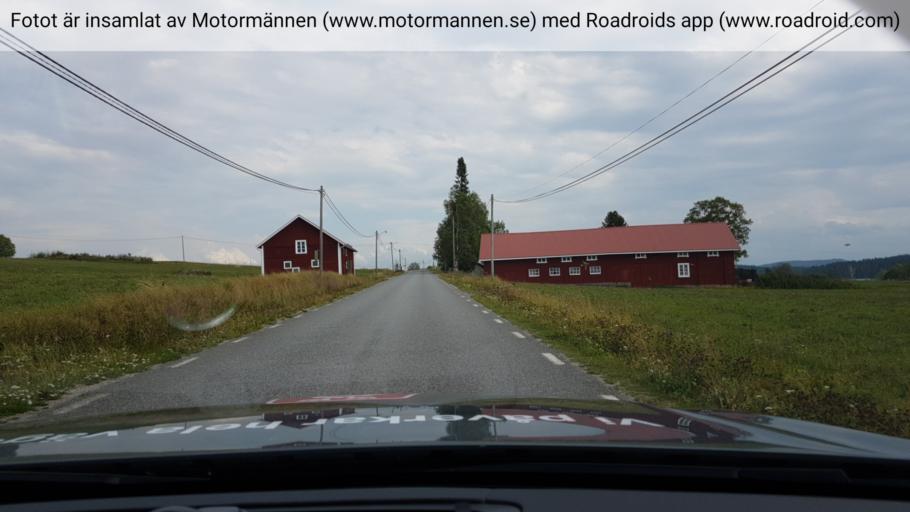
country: SE
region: Jaemtland
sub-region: OEstersunds Kommun
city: Brunflo
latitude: 62.9637
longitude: 15.1338
